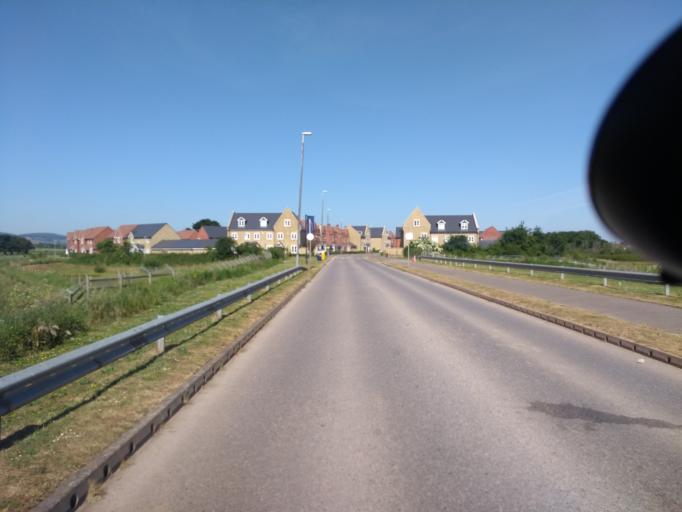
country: GB
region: England
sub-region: Somerset
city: North Petherton
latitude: 51.1085
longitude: -3.0073
